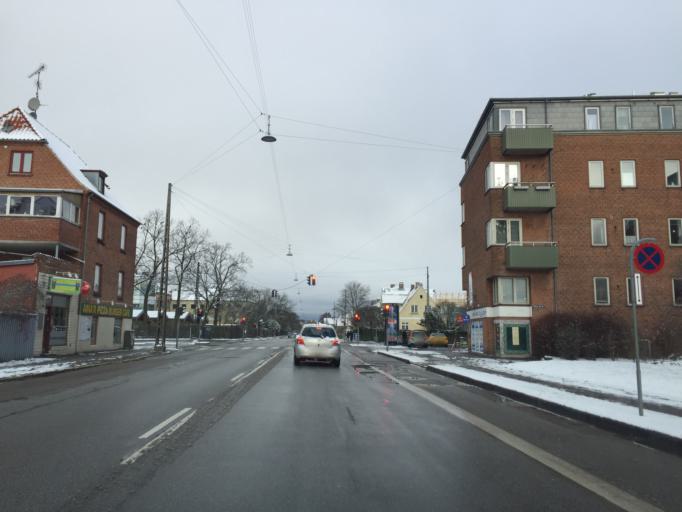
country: DK
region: Capital Region
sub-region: Tarnby Kommune
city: Tarnby
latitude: 55.6545
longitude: 12.6232
